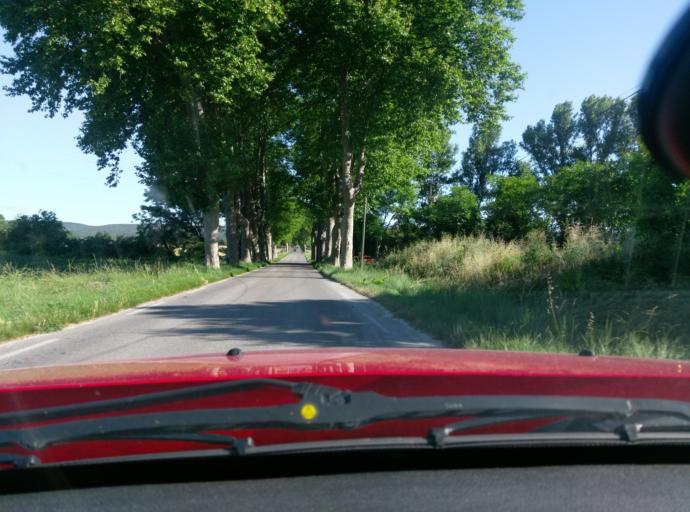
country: FR
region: Languedoc-Roussillon
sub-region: Departement du Gard
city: Uzes
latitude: 44.0325
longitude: 4.4104
